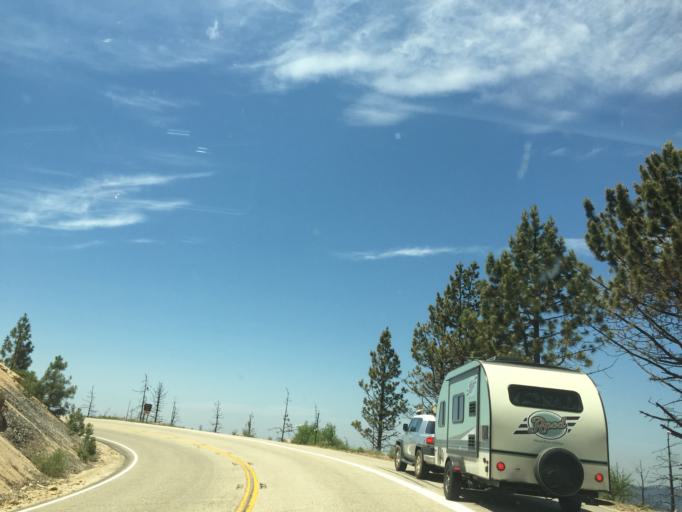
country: US
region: California
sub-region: Fresno County
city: Squaw Valley
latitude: 36.7752
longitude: -118.9606
